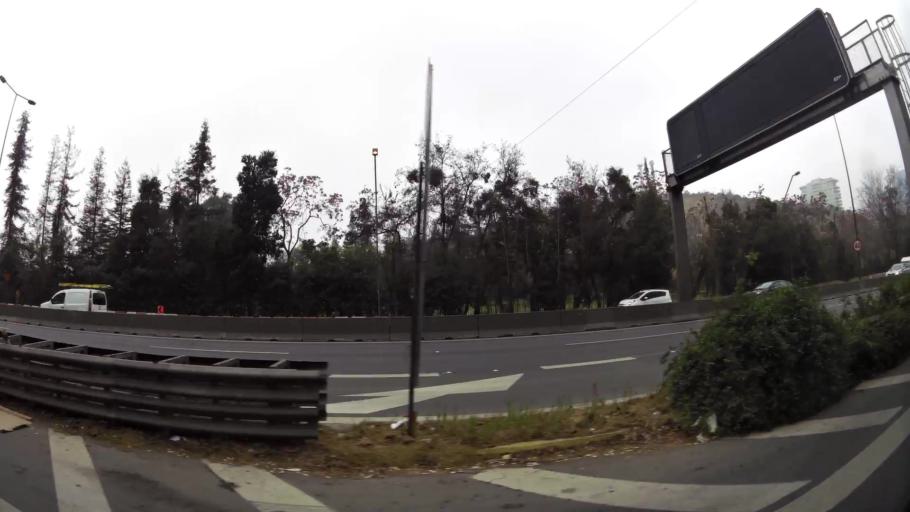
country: CL
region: Santiago Metropolitan
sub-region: Provincia de Santiago
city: Villa Presidente Frei, Nunoa, Santiago, Chile
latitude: -33.4076
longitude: -70.5980
